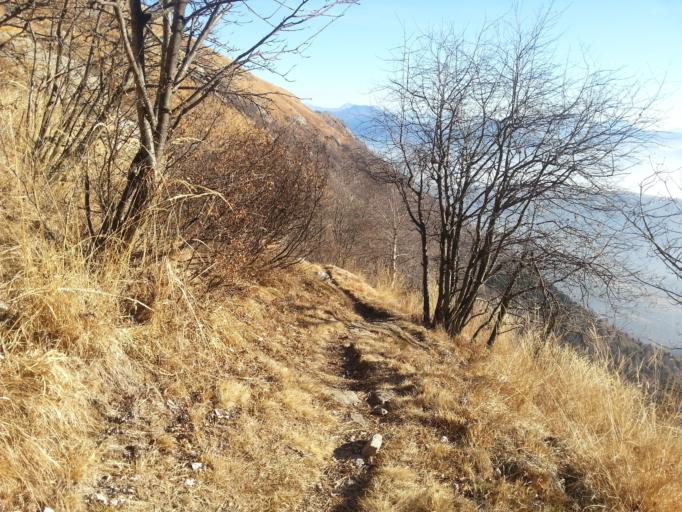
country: IT
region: Lombardy
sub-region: Provincia di Varese
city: Curiglia
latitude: 46.0436
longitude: 8.8394
